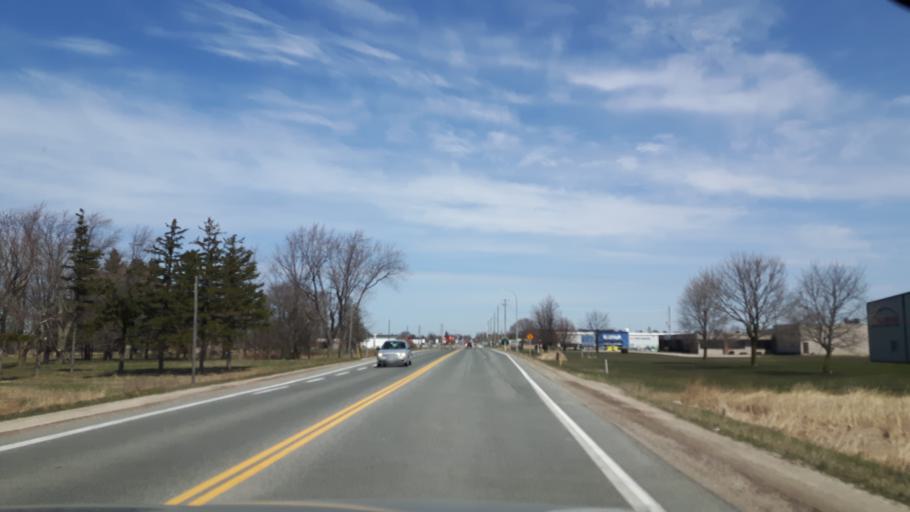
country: CA
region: Ontario
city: Goderich
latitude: 43.7246
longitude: -81.7058
